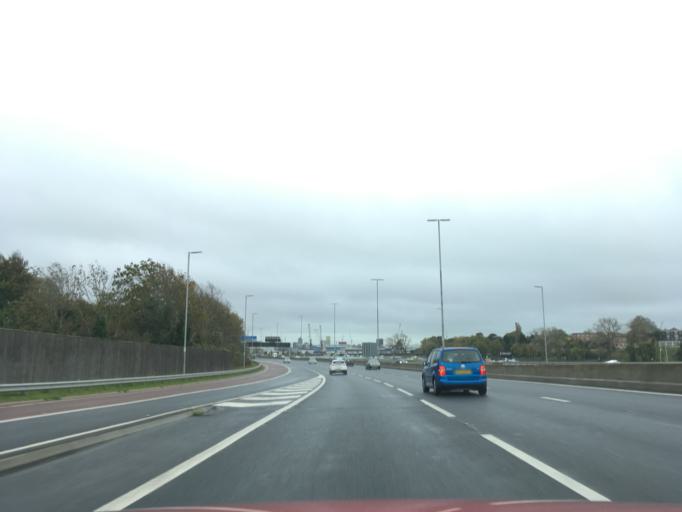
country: GB
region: England
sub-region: Portsmouth
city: Portsmouth
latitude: 50.8223
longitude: -1.0928
